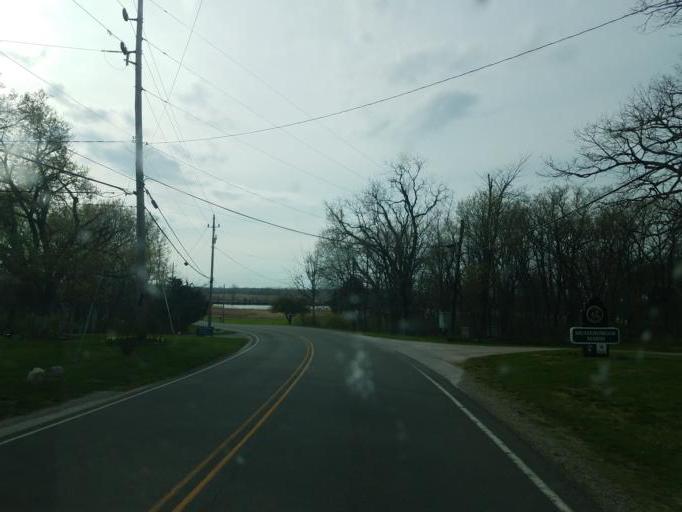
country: US
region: Ohio
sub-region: Erie County
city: Sandusky
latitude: 41.5061
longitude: -82.7698
